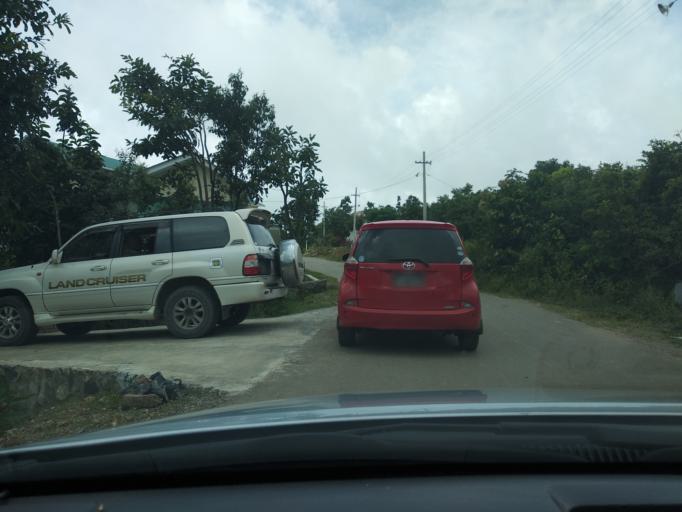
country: MM
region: Mandalay
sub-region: Pyin Oo Lwin District
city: Pyin Oo Lwin
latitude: 21.9143
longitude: 96.3861
